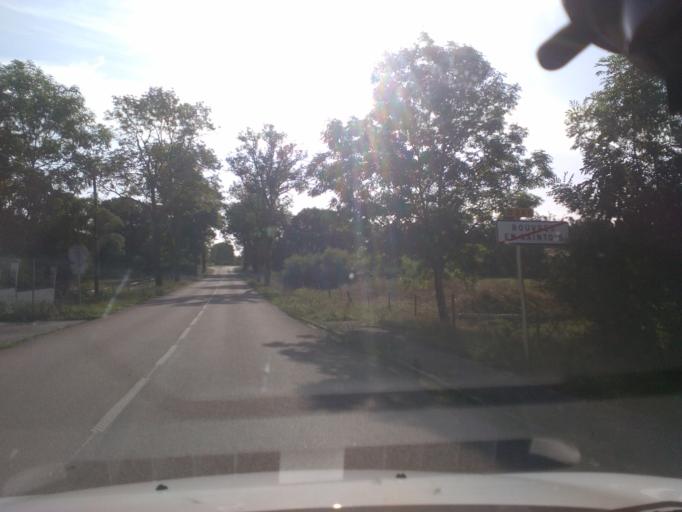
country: FR
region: Lorraine
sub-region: Departement des Vosges
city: Mirecourt
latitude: 48.3082
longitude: 6.0378
